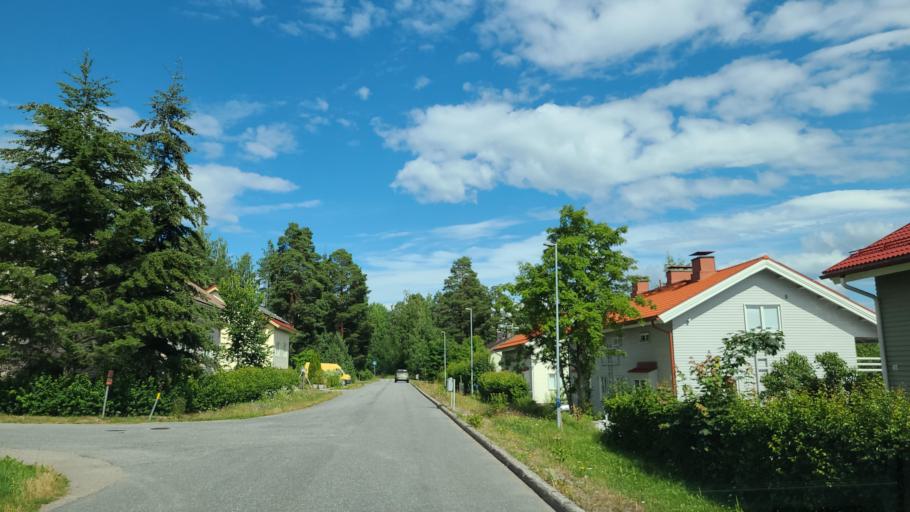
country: FI
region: Central Finland
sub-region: Jyvaeskylae
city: Saeynaetsalo
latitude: 62.2485
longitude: 25.8742
